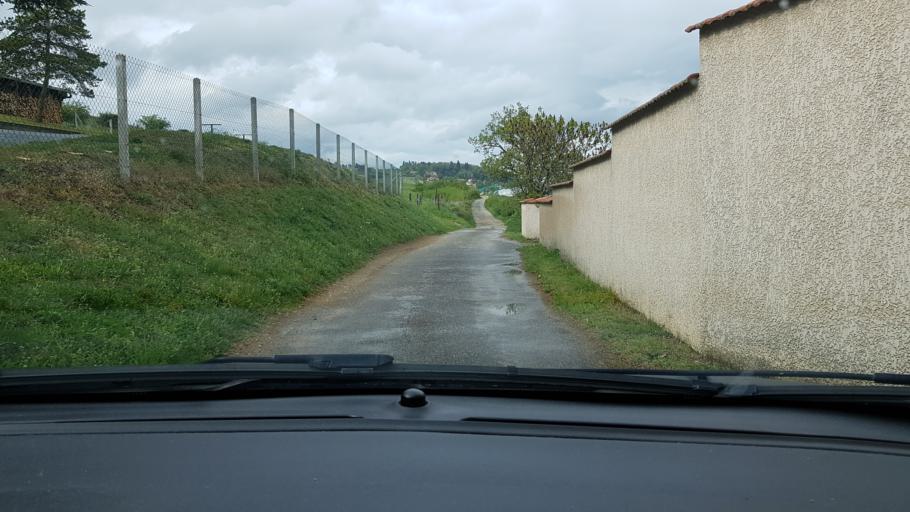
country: FR
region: Rhone-Alpes
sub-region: Departement du Rhone
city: Saint-Maurice-sur-Dargoire
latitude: 45.6050
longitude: 4.6318
